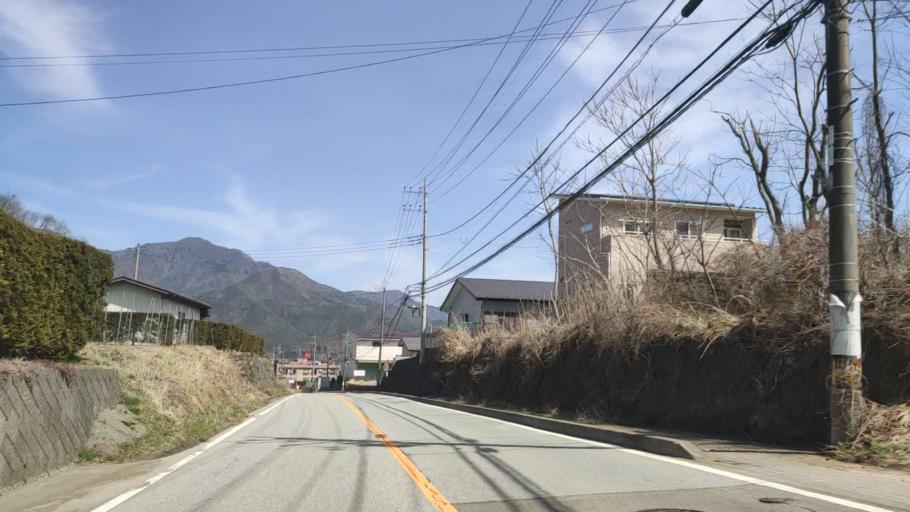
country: JP
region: Yamanashi
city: Fujikawaguchiko
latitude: 35.5005
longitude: 138.7367
